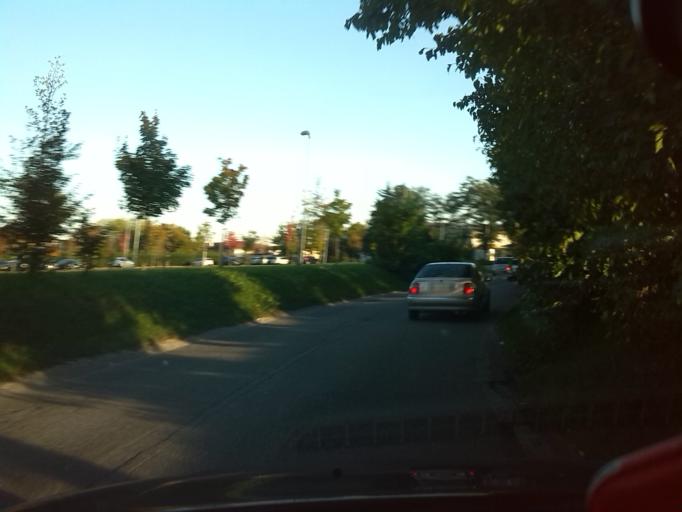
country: IT
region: Friuli Venezia Giulia
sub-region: Provincia di Udine
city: Basaldella
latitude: 46.0308
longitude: 13.2464
